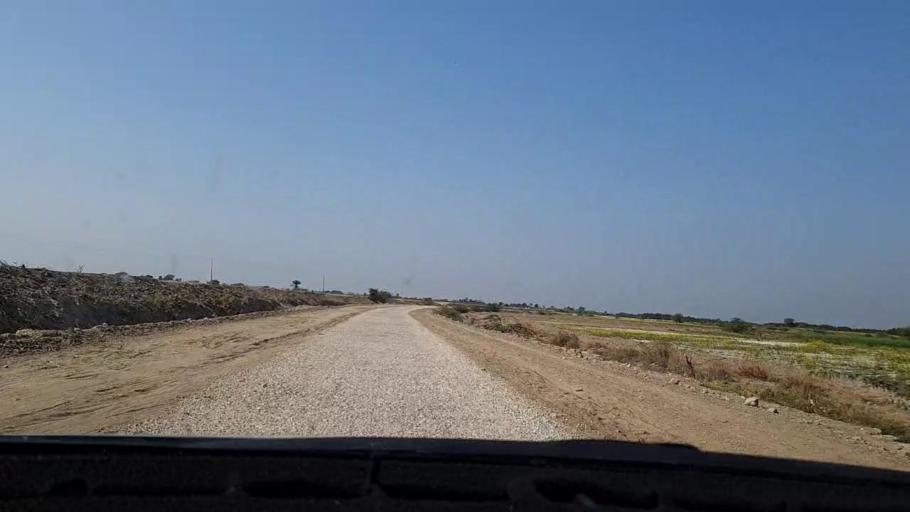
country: PK
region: Sindh
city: Tando Mittha Khan
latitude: 25.8199
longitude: 69.2952
